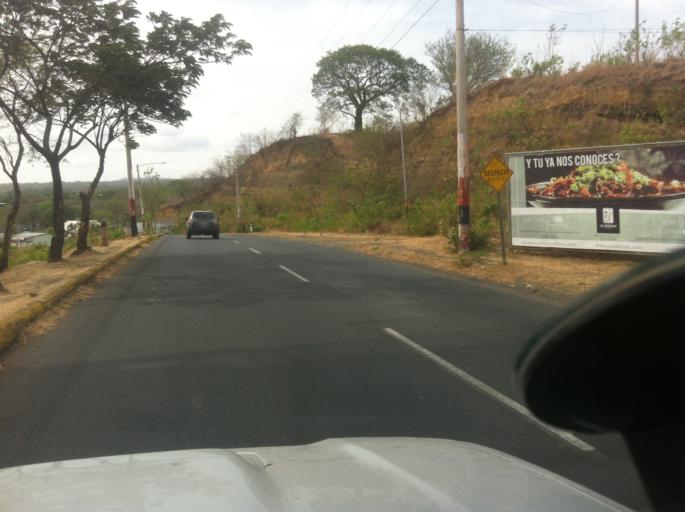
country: NI
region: Managua
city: Managua
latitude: 12.1089
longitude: -86.3026
